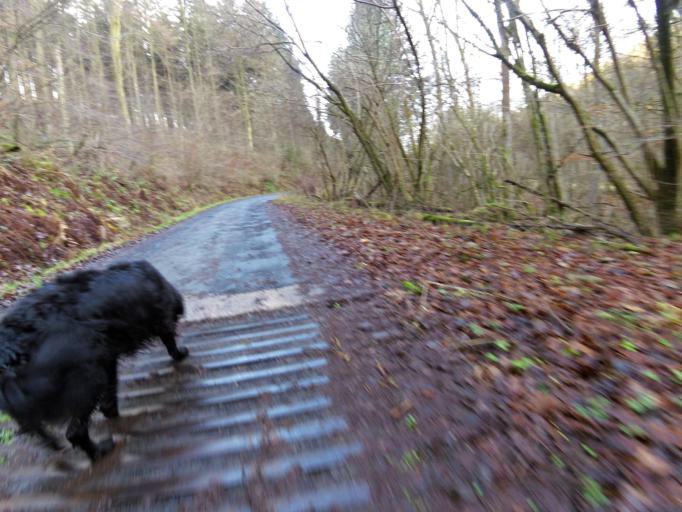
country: DE
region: Lower Saxony
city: Hannoversch Munden
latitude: 51.4650
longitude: 9.6075
